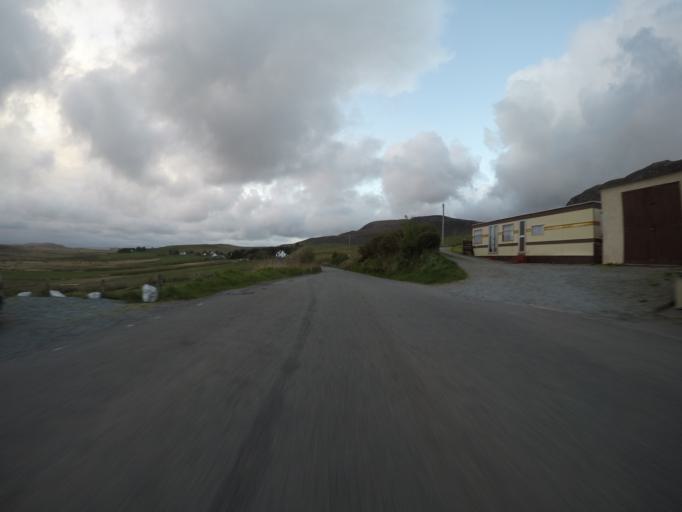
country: GB
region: Scotland
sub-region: Highland
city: Portree
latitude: 57.6124
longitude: -6.3714
